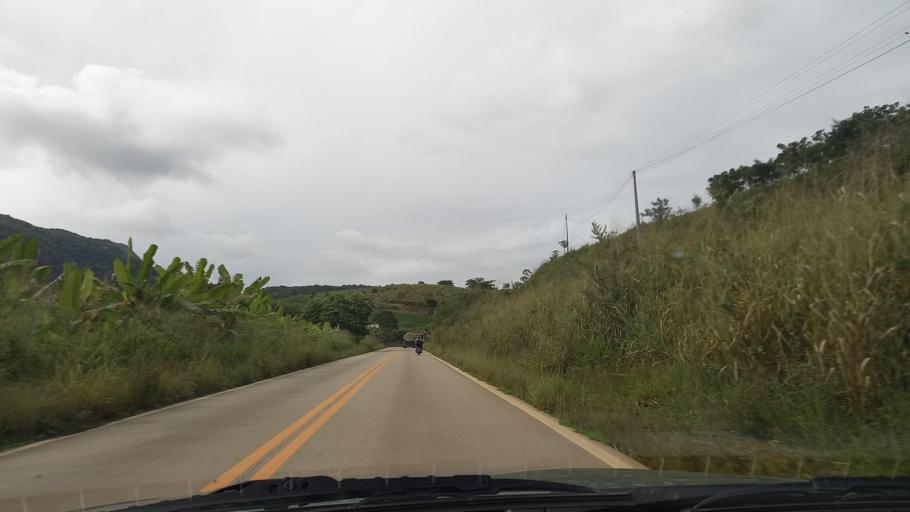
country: BR
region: Pernambuco
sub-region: Maraial
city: Maraial
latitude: -8.7563
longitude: -35.8481
